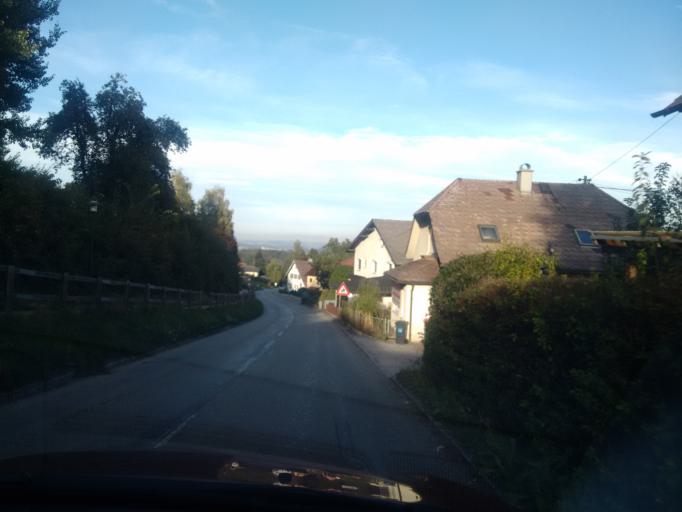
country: AT
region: Upper Austria
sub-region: Politischer Bezirk Vocklabruck
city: Wolfsegg am Hausruck
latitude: 48.1082
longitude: 13.6764
